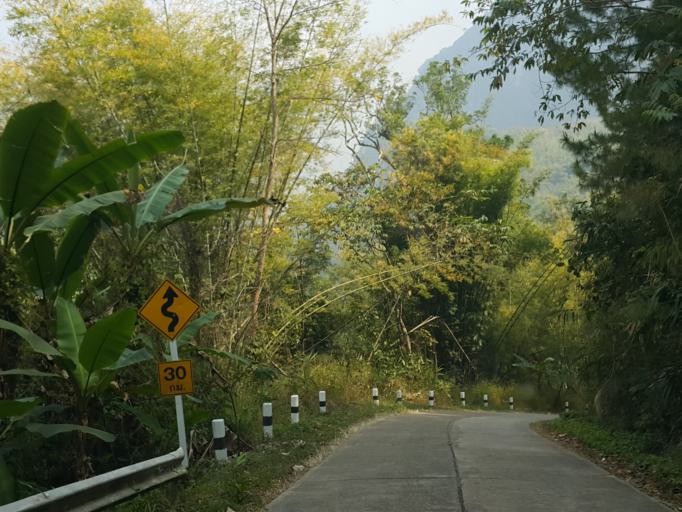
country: TH
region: Chiang Mai
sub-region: Amphoe Chiang Dao
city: Chiang Dao
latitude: 19.4125
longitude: 98.8571
